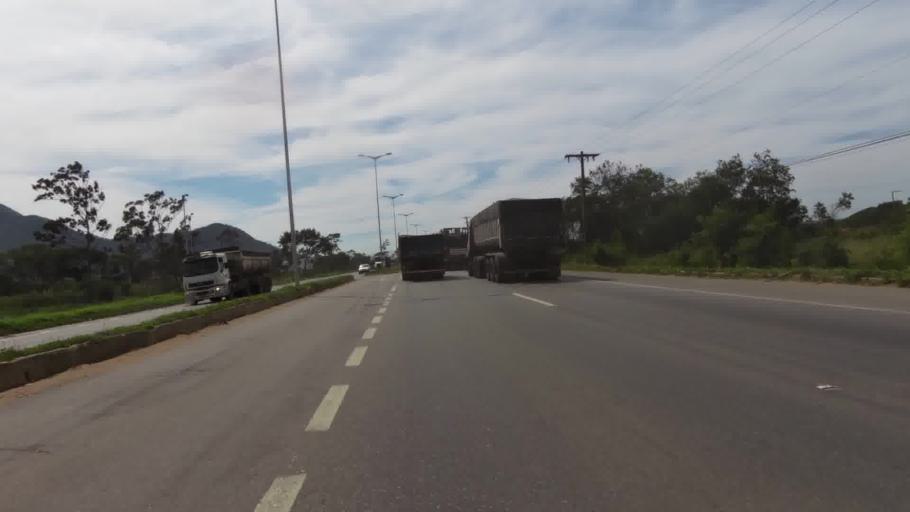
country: BR
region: Espirito Santo
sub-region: Serra
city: Serra
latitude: -20.2096
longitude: -40.3163
